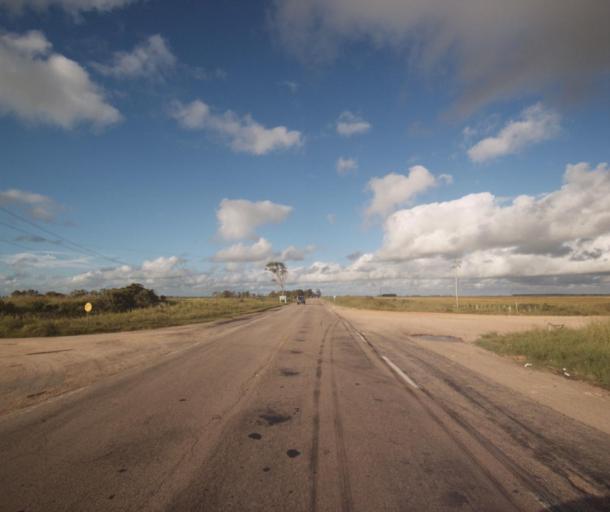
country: BR
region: Rio Grande do Sul
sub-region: Rio Grande
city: Rio Grande
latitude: -32.2102
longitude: -52.4543
